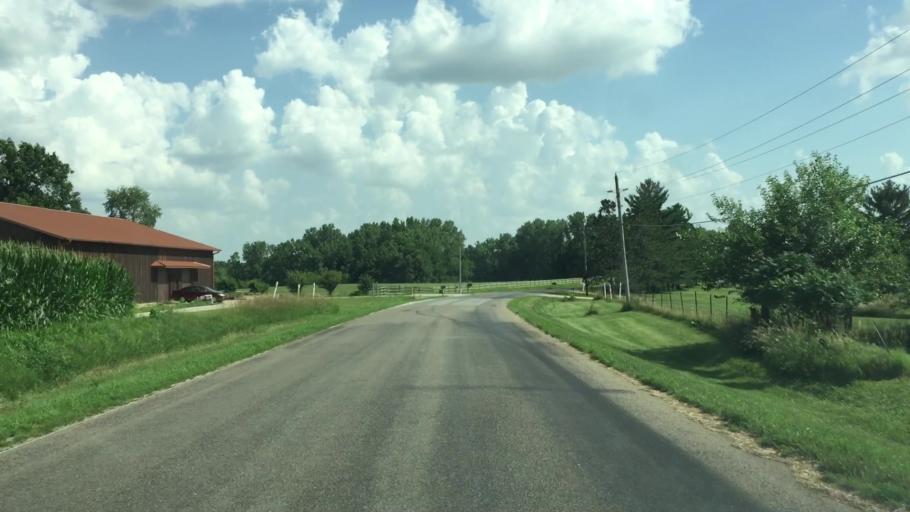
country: US
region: Iowa
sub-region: Johnson County
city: North Liberty
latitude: 41.8122
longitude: -91.6149
